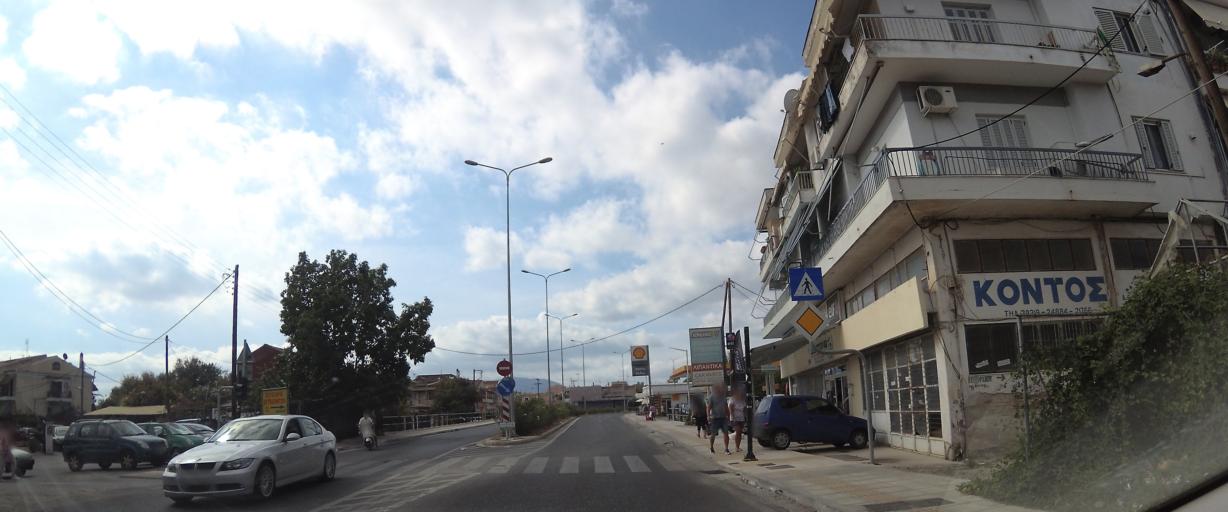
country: GR
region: Ionian Islands
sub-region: Nomos Kerkyras
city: Kerkyra
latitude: 39.6167
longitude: 19.9140
